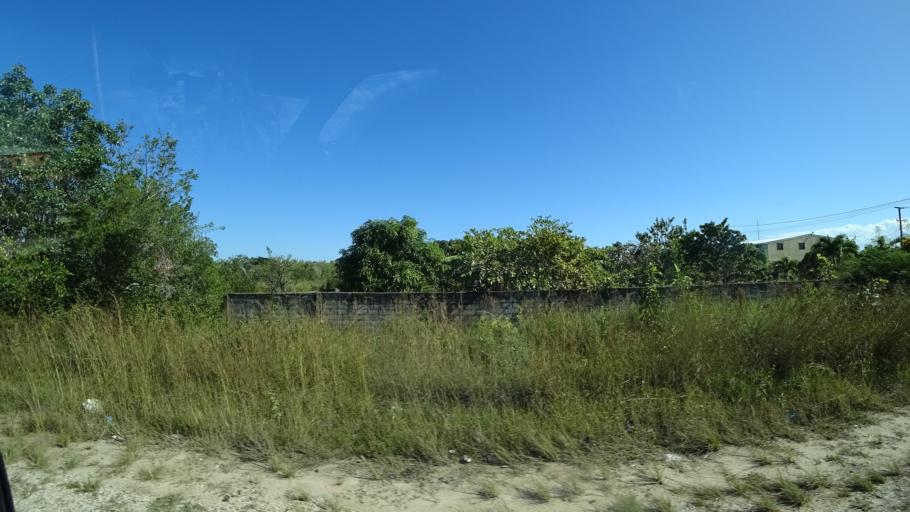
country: BZ
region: Belize
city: Belize City
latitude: 17.5618
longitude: -88.3227
